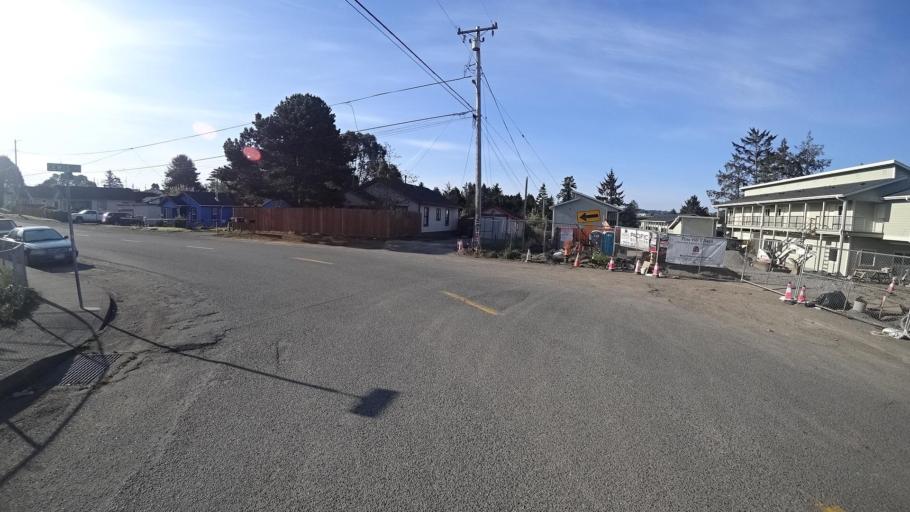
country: US
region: California
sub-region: Humboldt County
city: Bayview
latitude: 40.7656
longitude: -124.1806
